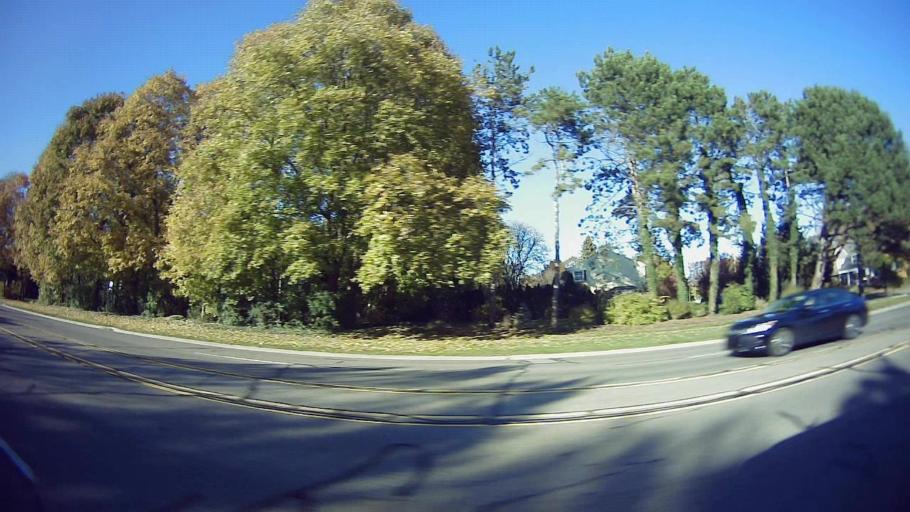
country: US
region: Michigan
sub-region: Oakland County
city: Beverly Hills
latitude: 42.5456
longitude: -83.2515
